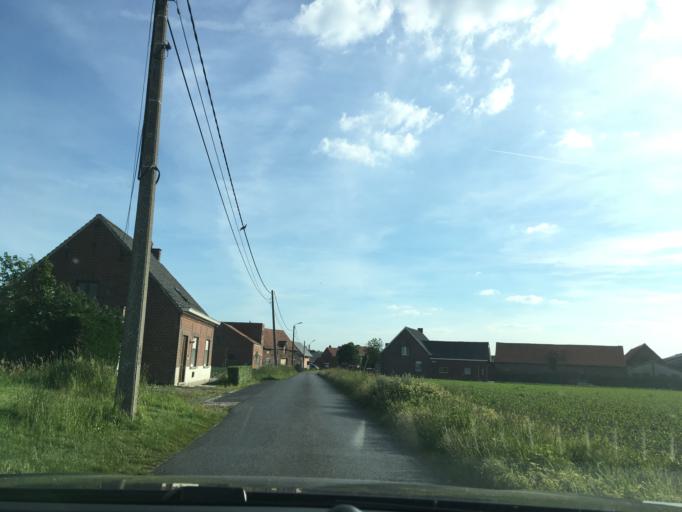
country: BE
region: Flanders
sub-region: Provincie West-Vlaanderen
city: Hooglede
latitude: 50.9451
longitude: 3.0681
